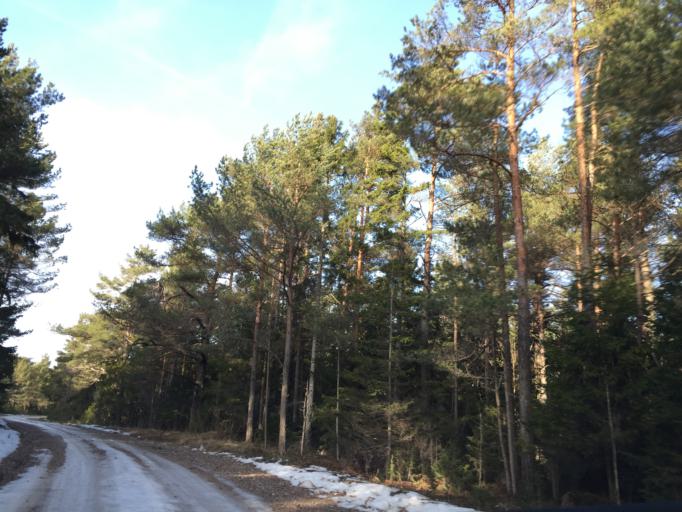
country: EE
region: Saare
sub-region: Kuressaare linn
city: Kuressaare
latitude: 58.4764
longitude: 21.9539
